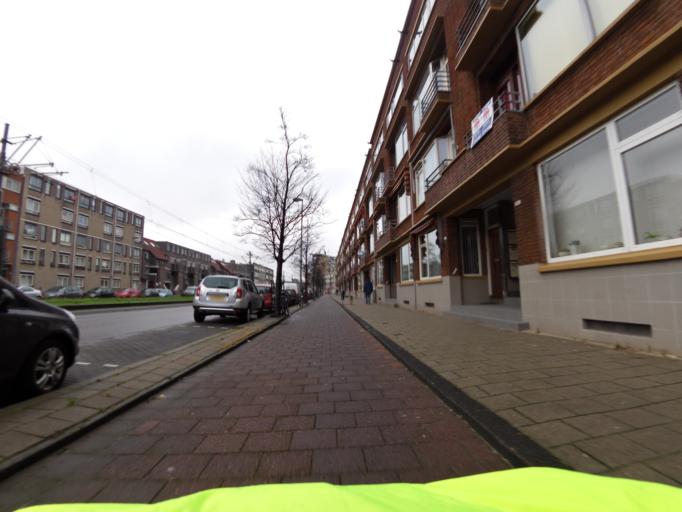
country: NL
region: South Holland
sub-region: Gemeente Schiedam
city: Schiedam
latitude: 51.9148
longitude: 4.4066
